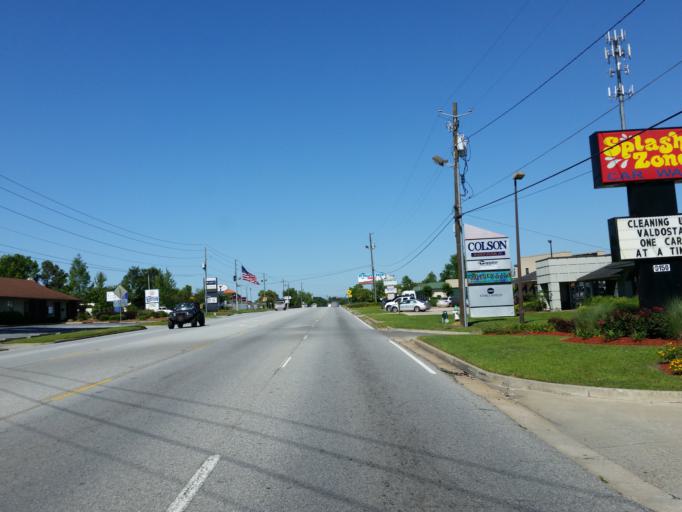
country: US
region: Georgia
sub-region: Lowndes County
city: Remerton
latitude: 30.8803
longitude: -83.2952
